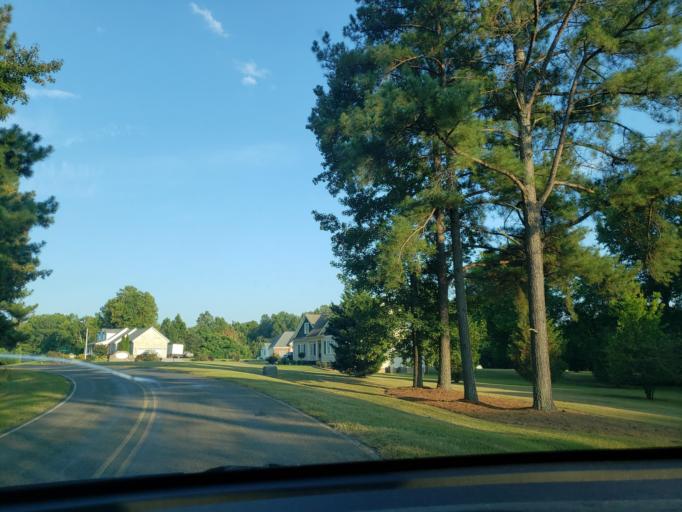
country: US
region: North Carolina
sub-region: Vance County
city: Henderson
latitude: 36.4013
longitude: -78.3742
